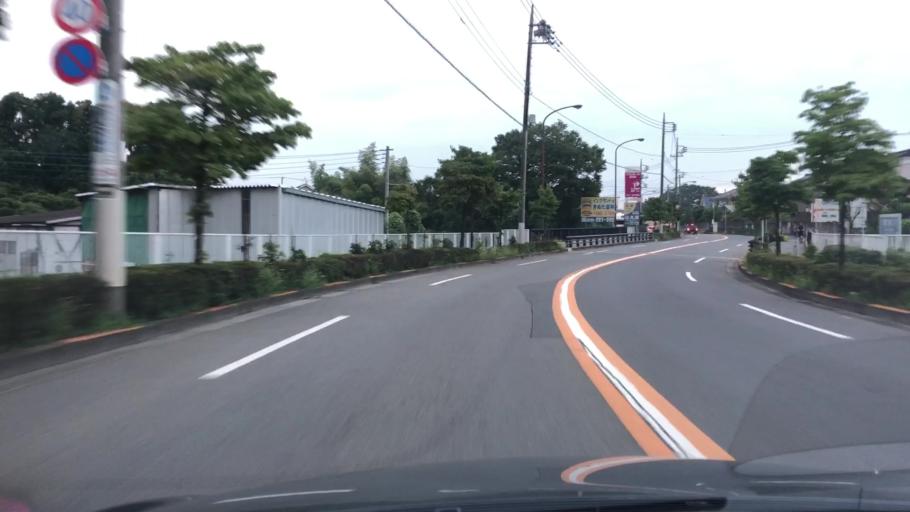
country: JP
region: Tokyo
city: Ome
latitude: 35.7413
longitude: 139.2640
